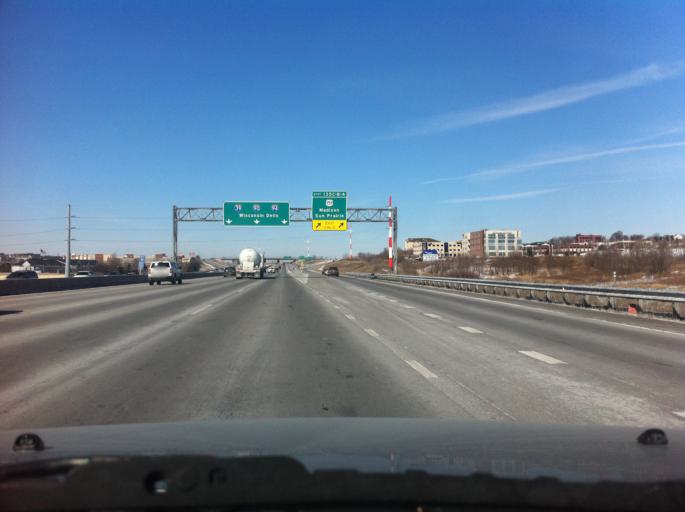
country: US
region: Wisconsin
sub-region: Dane County
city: Monona
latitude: 43.1094
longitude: -89.2839
